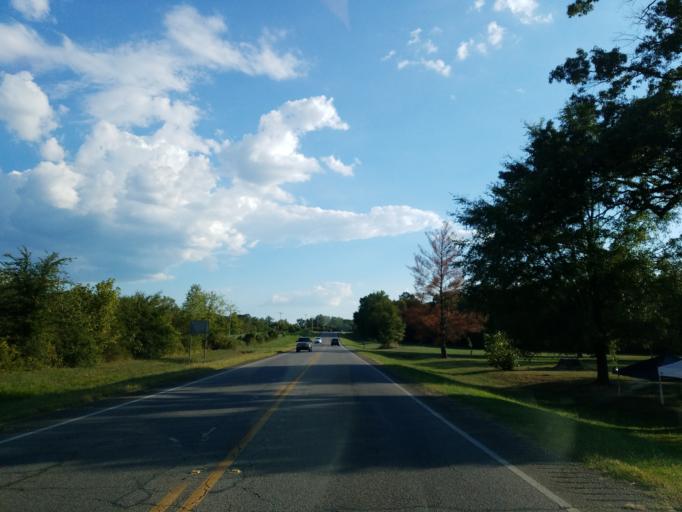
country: US
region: Georgia
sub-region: Murray County
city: Chatsworth
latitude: 34.8846
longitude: -84.7502
